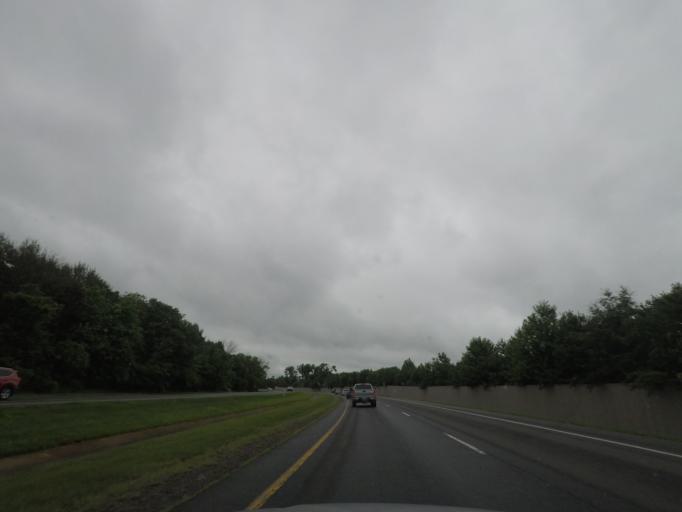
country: US
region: Virginia
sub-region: Prince William County
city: Haymarket
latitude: 38.8322
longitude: -77.6328
